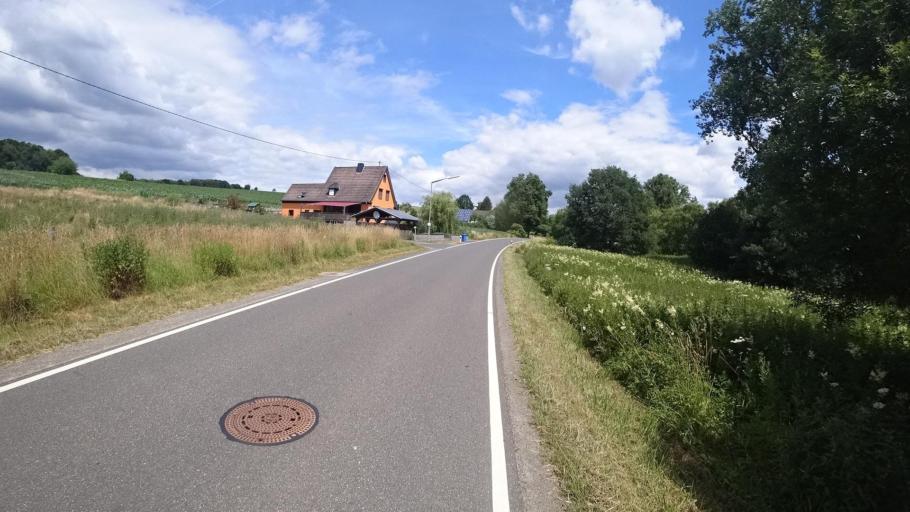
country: DE
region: Rheinland-Pfalz
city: Ersfeld
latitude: 50.6969
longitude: 7.5229
